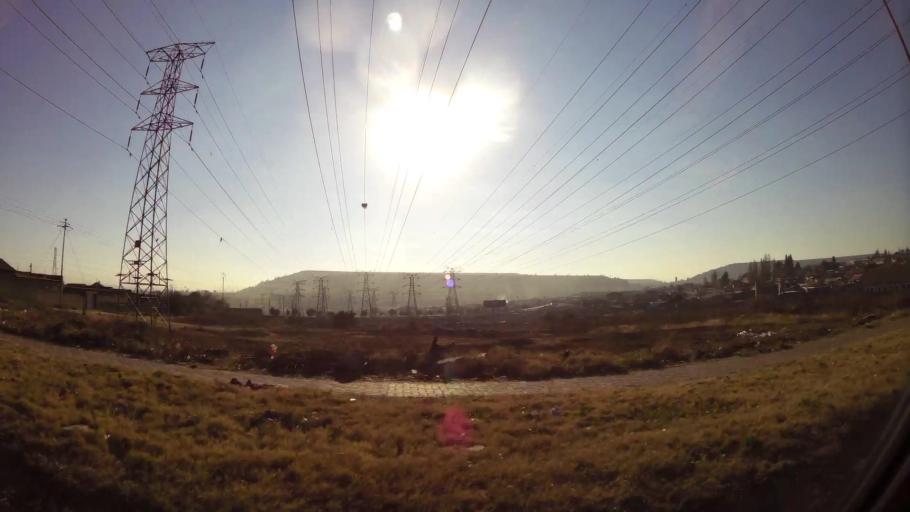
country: ZA
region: Gauteng
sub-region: City of Johannesburg Metropolitan Municipality
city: Soweto
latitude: -26.2358
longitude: 27.9408
